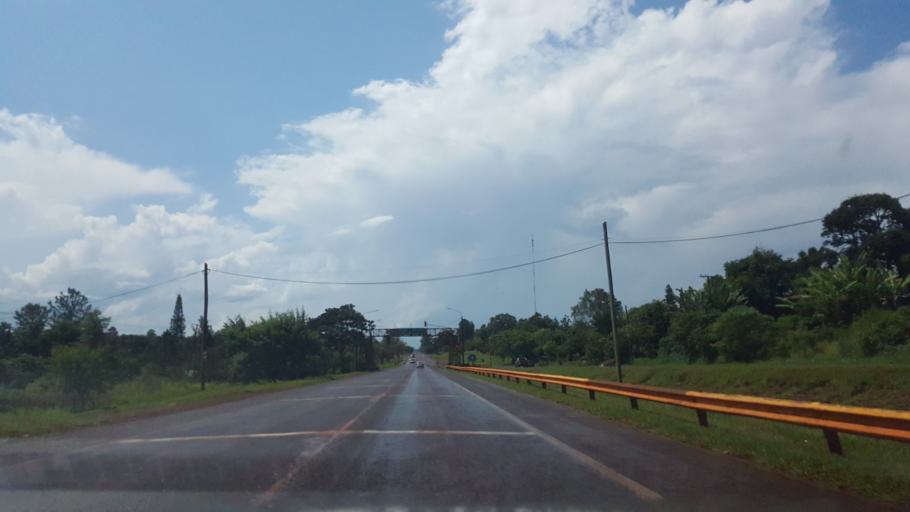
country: AR
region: Misiones
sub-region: Departamento de Eldorado
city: Eldorado
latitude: -26.3963
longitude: -54.6325
